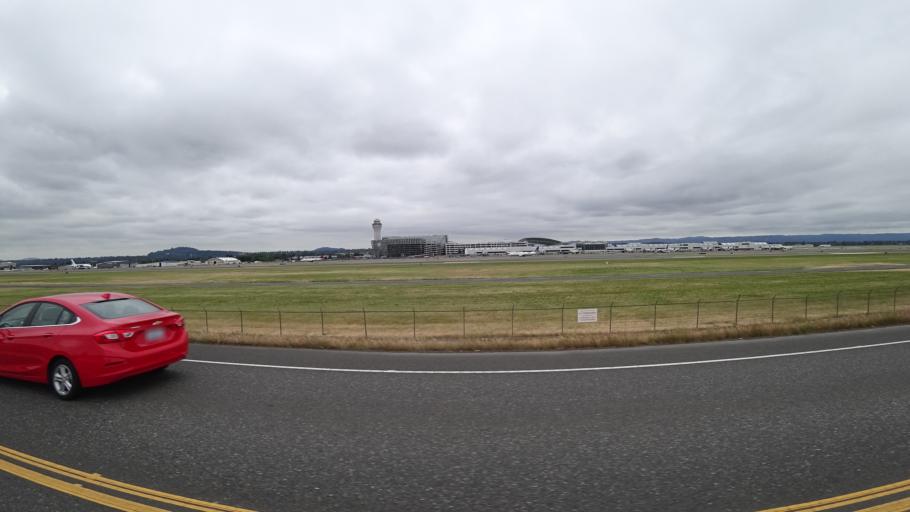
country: US
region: Washington
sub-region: Clark County
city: Walnut Grove
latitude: 45.5940
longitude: -122.5871
